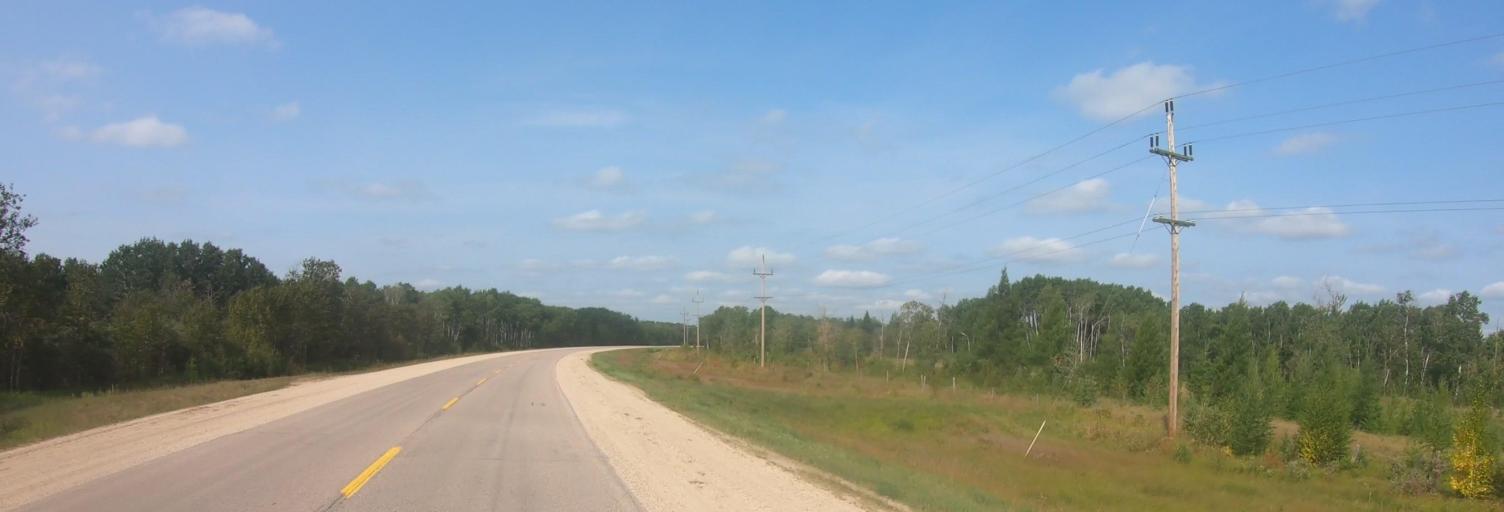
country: CA
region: Manitoba
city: La Broquerie
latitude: 49.1777
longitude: -96.2219
